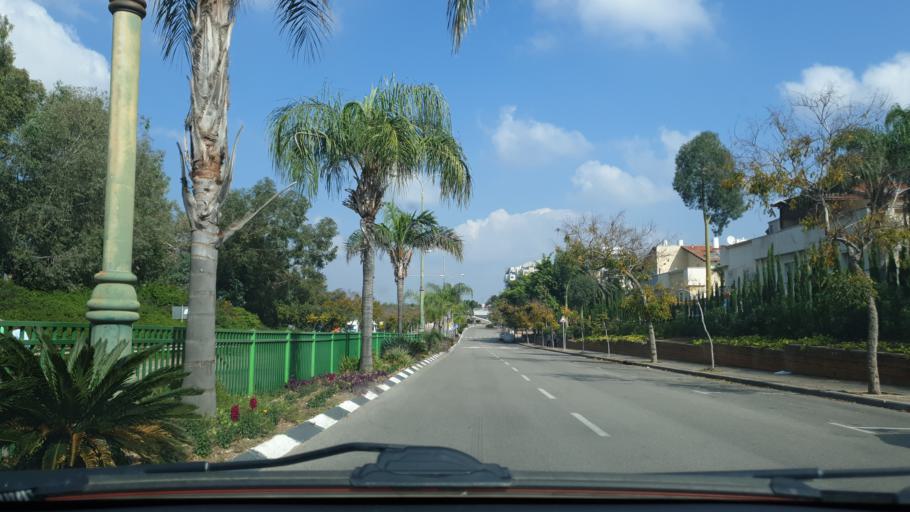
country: IL
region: Central District
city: Rishon LeZiyyon
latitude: 31.9682
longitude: 34.8183
